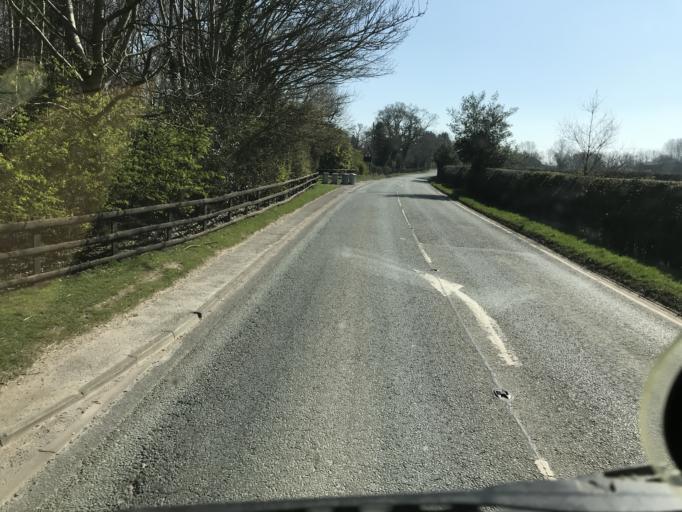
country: GB
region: England
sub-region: Cheshire East
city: Mobberley
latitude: 53.2794
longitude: -2.3055
